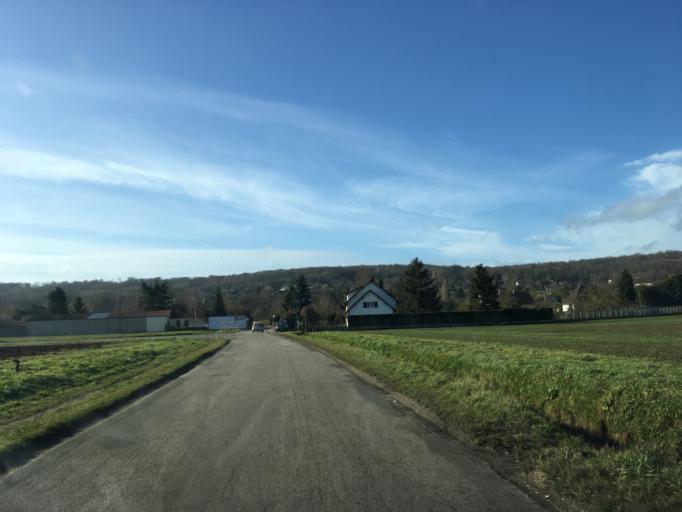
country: FR
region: Haute-Normandie
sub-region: Departement de l'Eure
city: Saint-Just
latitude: 49.1111
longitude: 1.4459
